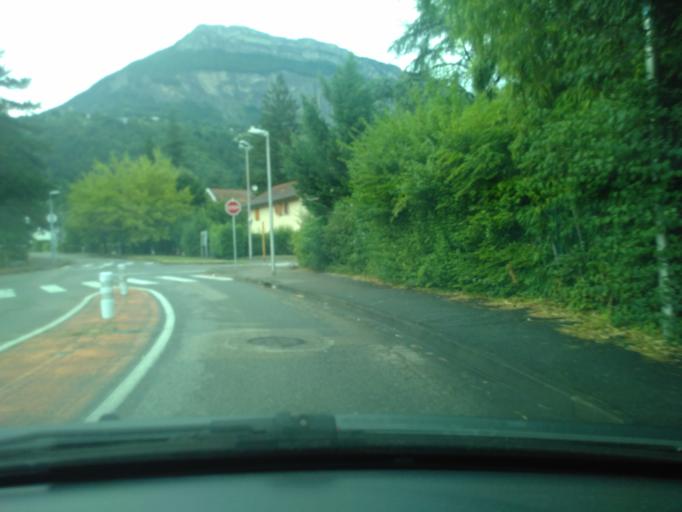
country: FR
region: Rhone-Alpes
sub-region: Departement de l'Isere
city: Corenc
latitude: 45.2098
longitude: 5.7675
